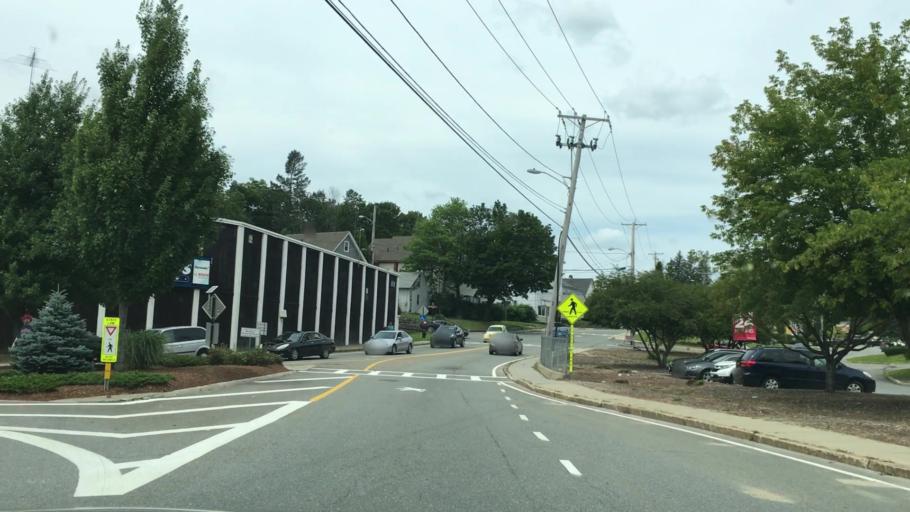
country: US
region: Massachusetts
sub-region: Worcester County
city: Gardner
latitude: 42.5700
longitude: -71.9929
